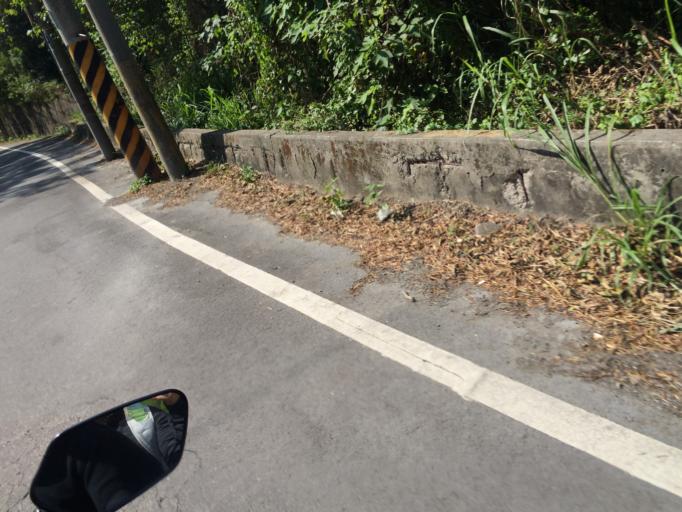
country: TW
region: Taiwan
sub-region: Hsinchu
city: Hsinchu
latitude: 24.7593
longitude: 120.9486
